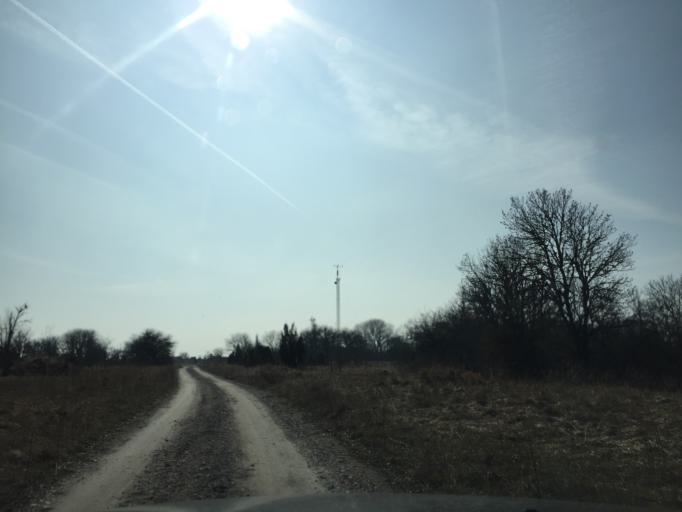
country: LV
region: Dundaga
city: Dundaga
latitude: 57.9202
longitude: 22.0600
